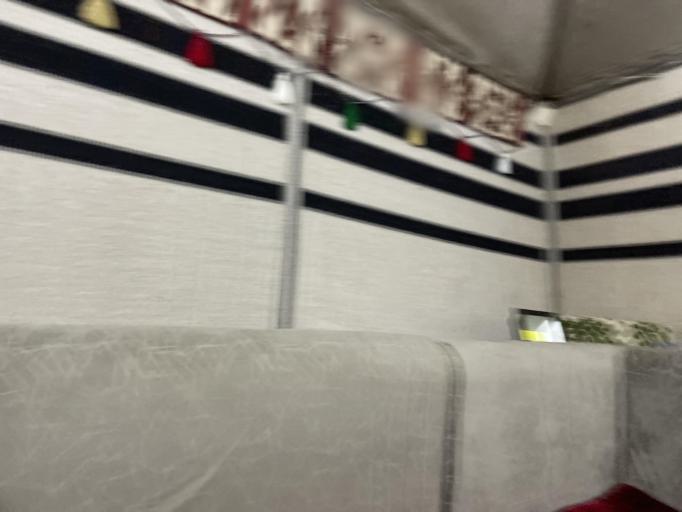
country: SA
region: Eastern Province
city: Al Qaysumah
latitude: 28.4903
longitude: 45.8559
